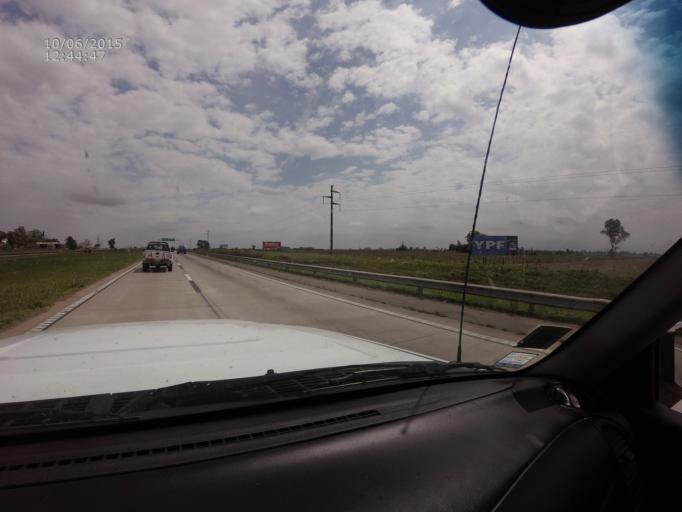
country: AR
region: Santa Fe
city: Canada de Gomez
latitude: -32.8495
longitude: -61.3737
